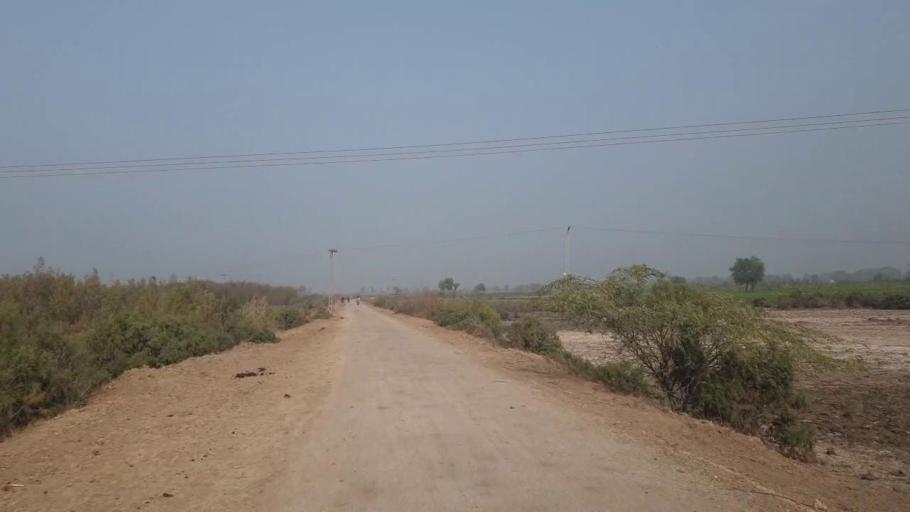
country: PK
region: Sindh
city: Bhit Shah
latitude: 25.8042
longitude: 68.5415
